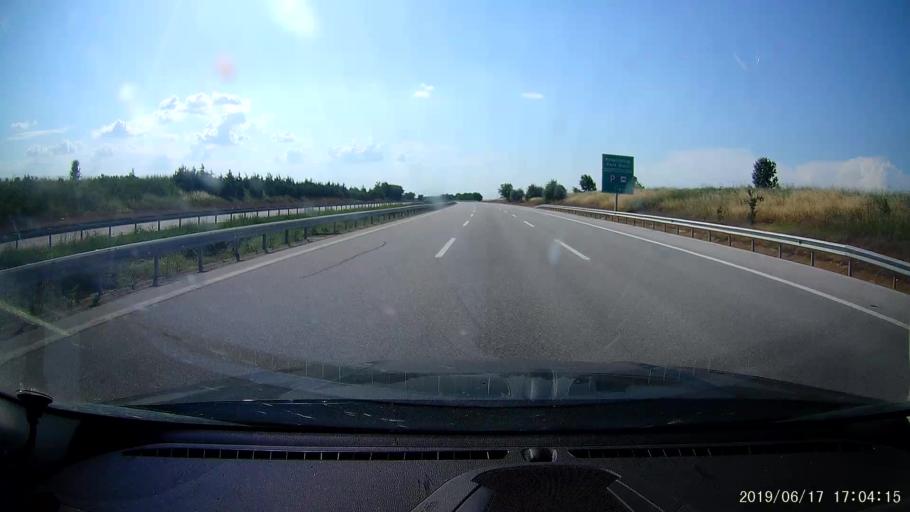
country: TR
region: Edirne
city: Haskoy
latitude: 41.6531
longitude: 26.7325
